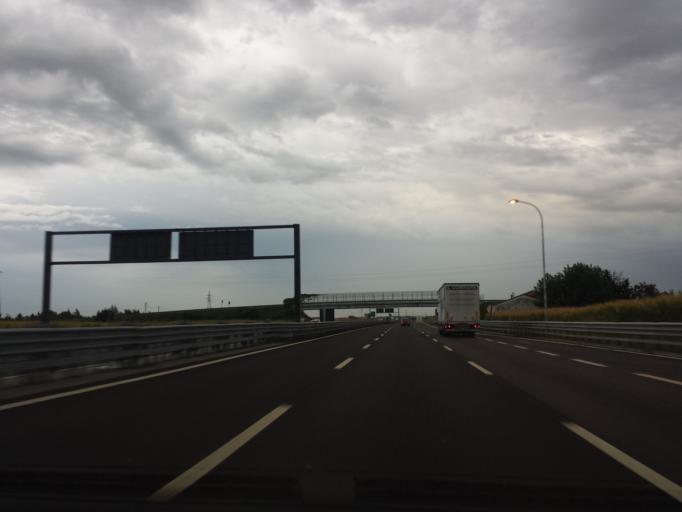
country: IT
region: Veneto
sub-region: Provincia di Vicenza
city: Torri di Quartesolo
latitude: 45.5040
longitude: 11.6274
